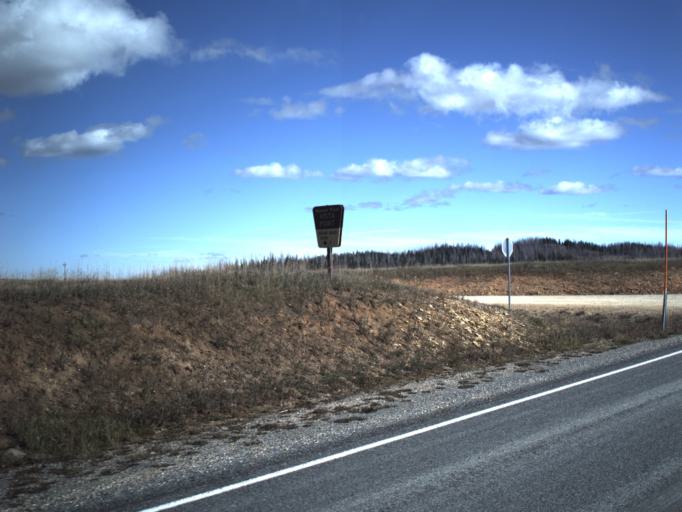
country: US
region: Utah
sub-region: Iron County
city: Parowan
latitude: 37.6692
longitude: -112.8396
